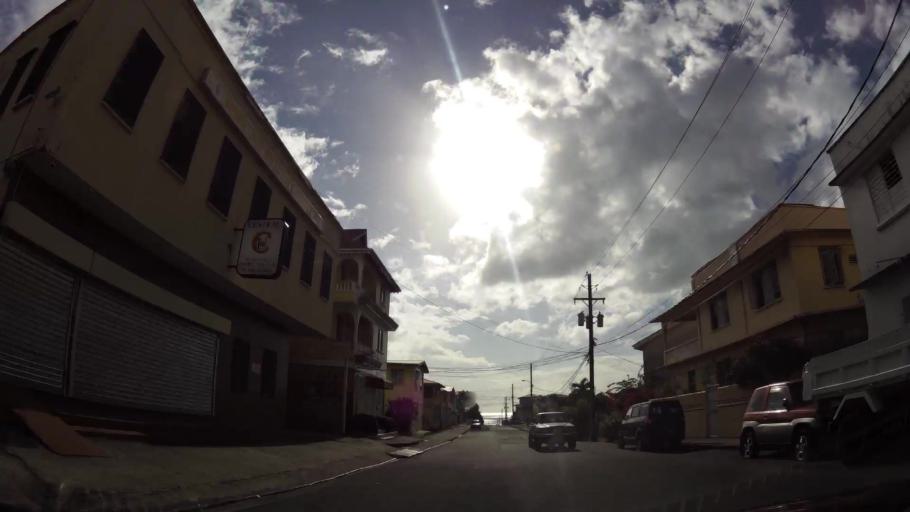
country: DM
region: Saint George
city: Roseau
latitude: 15.3046
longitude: -61.3864
